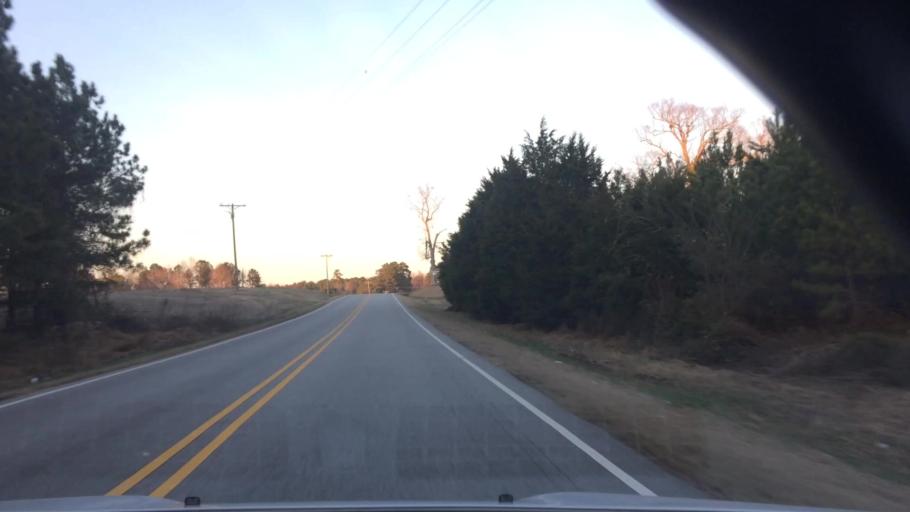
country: US
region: North Carolina
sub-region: Wake County
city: Rolesville
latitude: 35.9809
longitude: -78.4202
